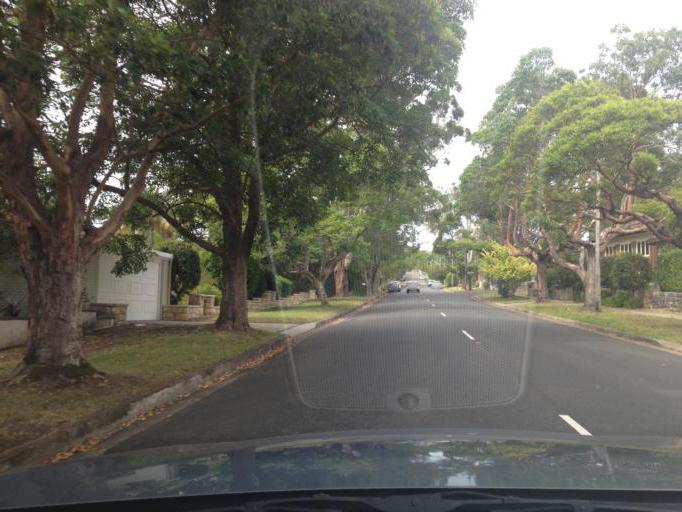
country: AU
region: New South Wales
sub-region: Ku-ring-gai
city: Killara
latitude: -33.7717
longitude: 151.1568
